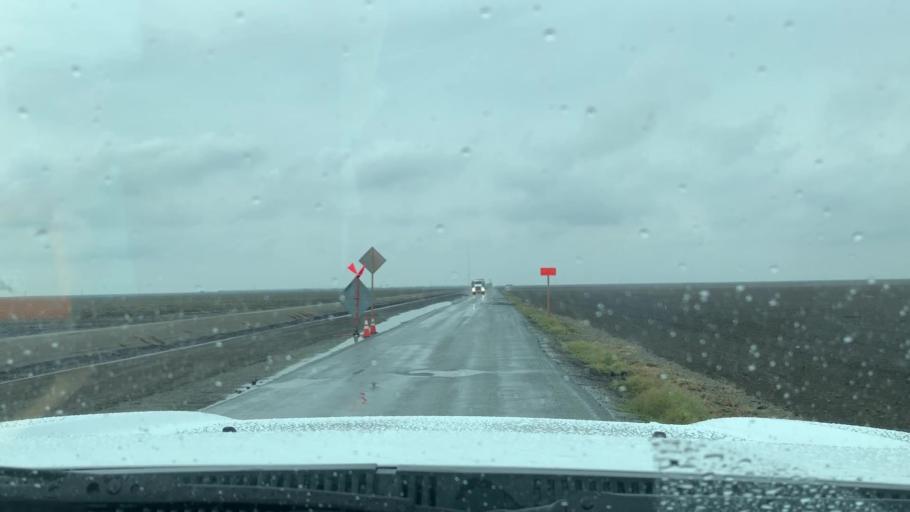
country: US
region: California
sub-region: Kings County
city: Corcoran
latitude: 36.0072
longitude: -119.5212
